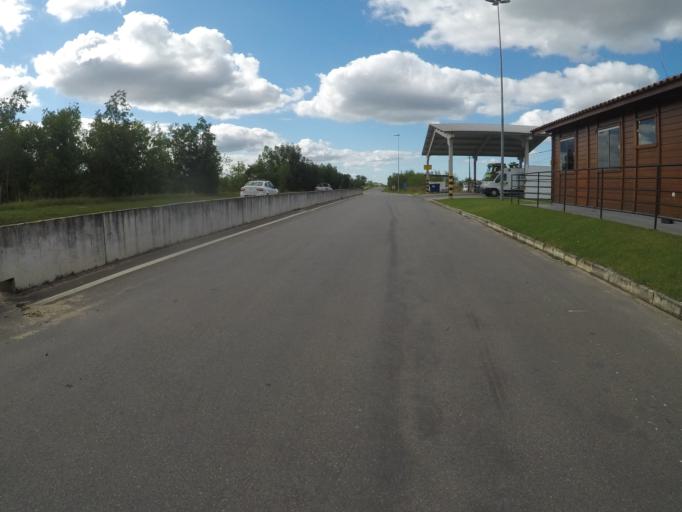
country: BR
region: Espirito Santo
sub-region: Linhares
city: Linhares
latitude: -19.1775
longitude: -40.0916
